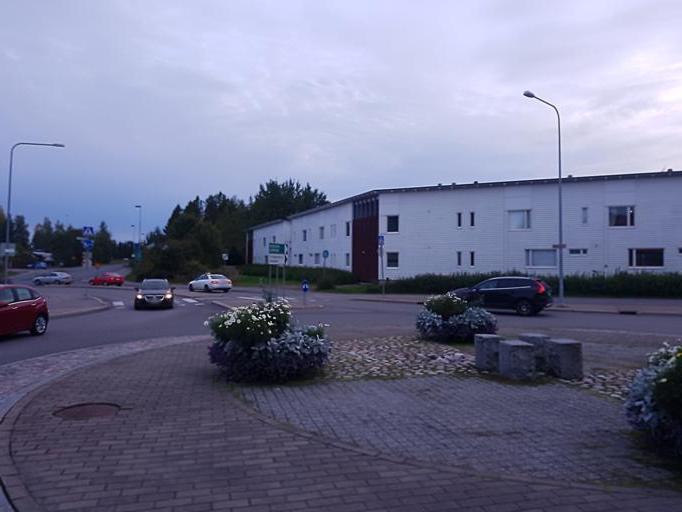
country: FI
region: Uusimaa
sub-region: Helsinki
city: Helsinki
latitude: 60.2562
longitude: 24.9485
